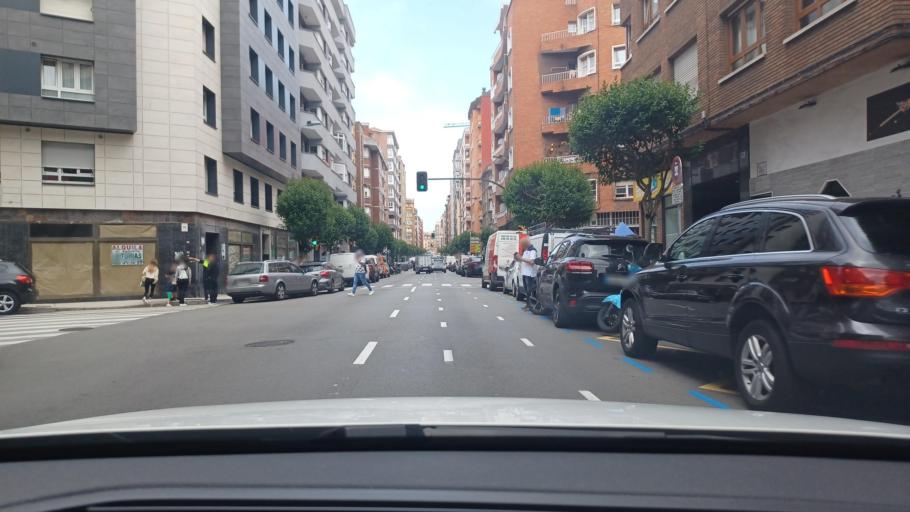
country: ES
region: Asturias
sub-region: Province of Asturias
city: Gijon
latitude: 43.5347
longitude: -5.6669
